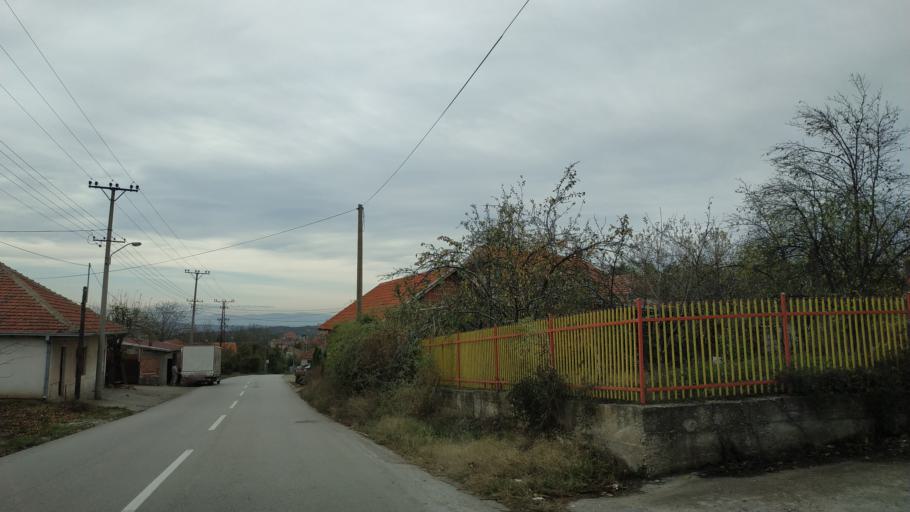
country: RS
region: Central Serbia
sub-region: Nisavski Okrug
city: Nis
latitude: 43.3603
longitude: 21.9559
